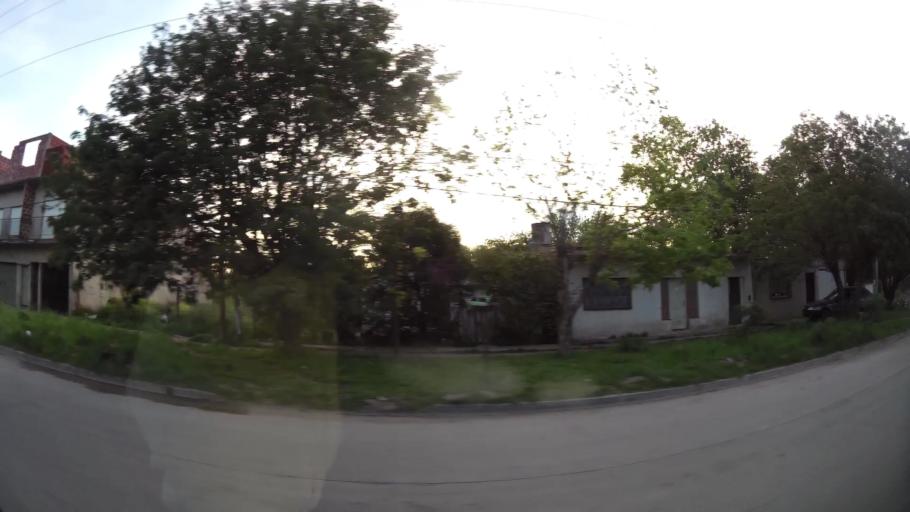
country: AR
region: Buenos Aires
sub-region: Partido de Almirante Brown
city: Adrogue
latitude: -34.8038
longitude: -58.2990
